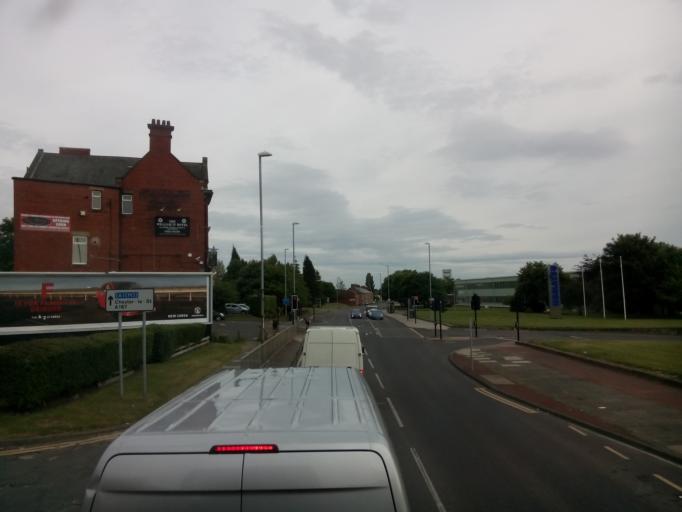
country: GB
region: England
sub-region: County Durham
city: Chester-le-Street
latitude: 54.8929
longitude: -1.5773
